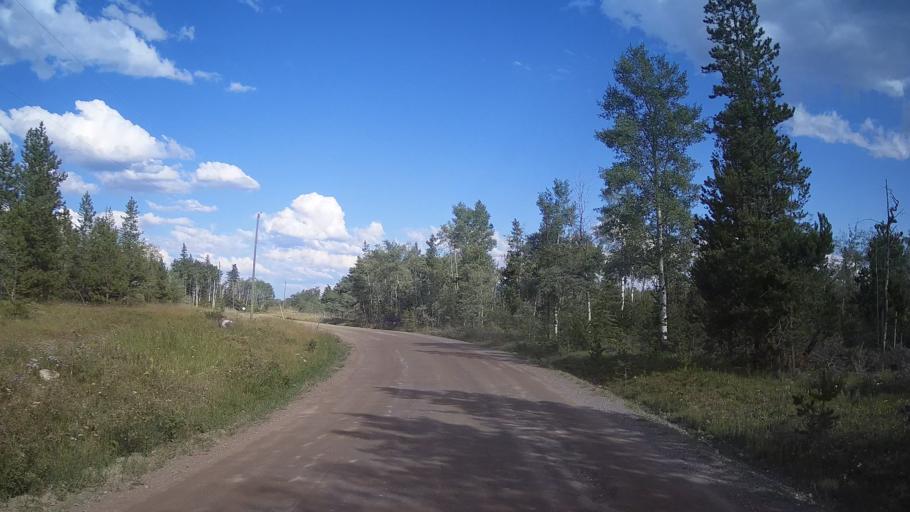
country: CA
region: British Columbia
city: Cache Creek
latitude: 51.2584
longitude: -121.6875
